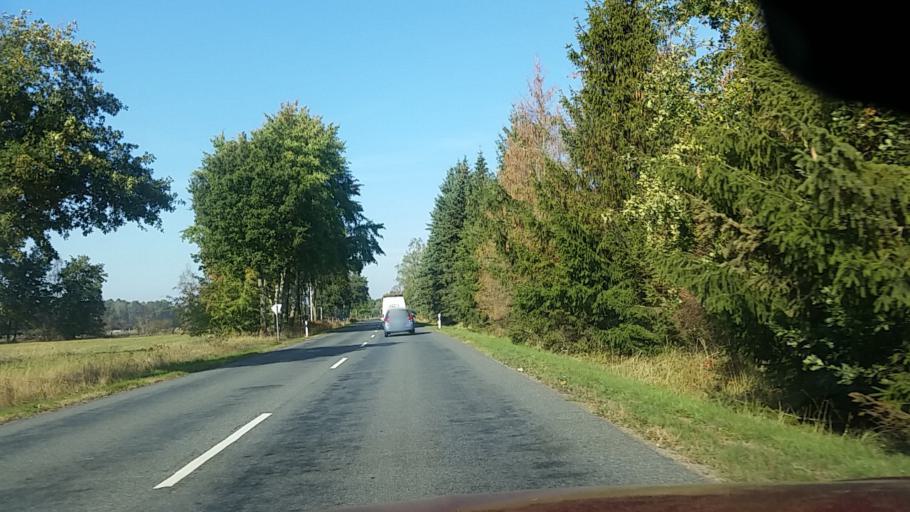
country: DE
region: Lower Saxony
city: Weyhausen
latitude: 52.4546
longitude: 10.7100
